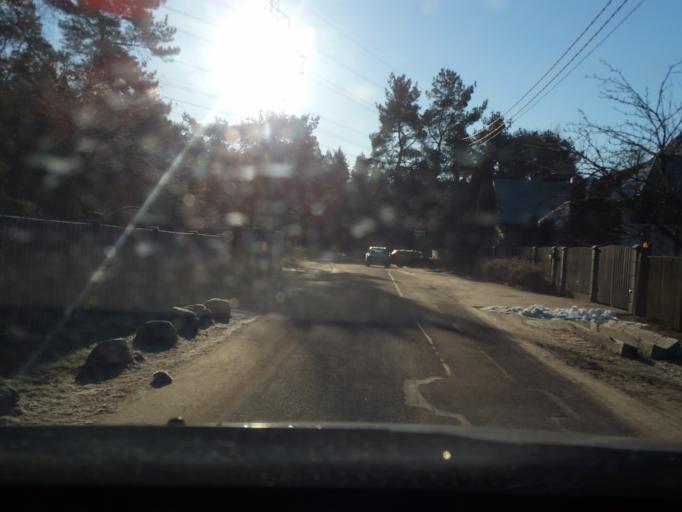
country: LV
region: Riga
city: Jaunciems
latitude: 56.9728
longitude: 24.1946
